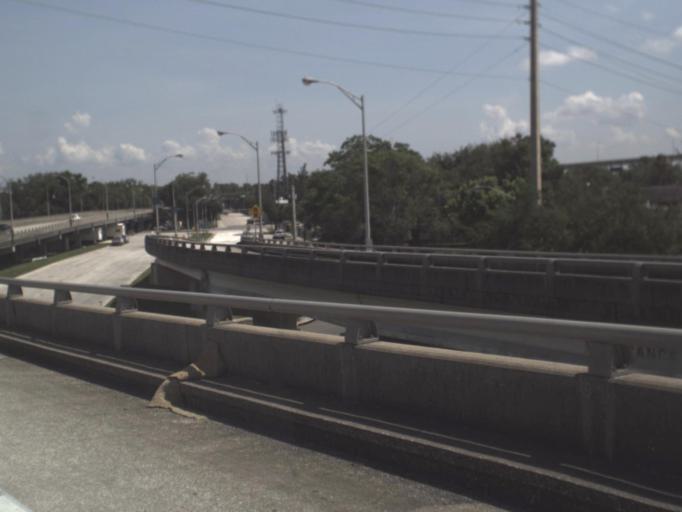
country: US
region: Florida
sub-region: Duval County
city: Jacksonville
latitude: 30.3221
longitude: -81.6344
